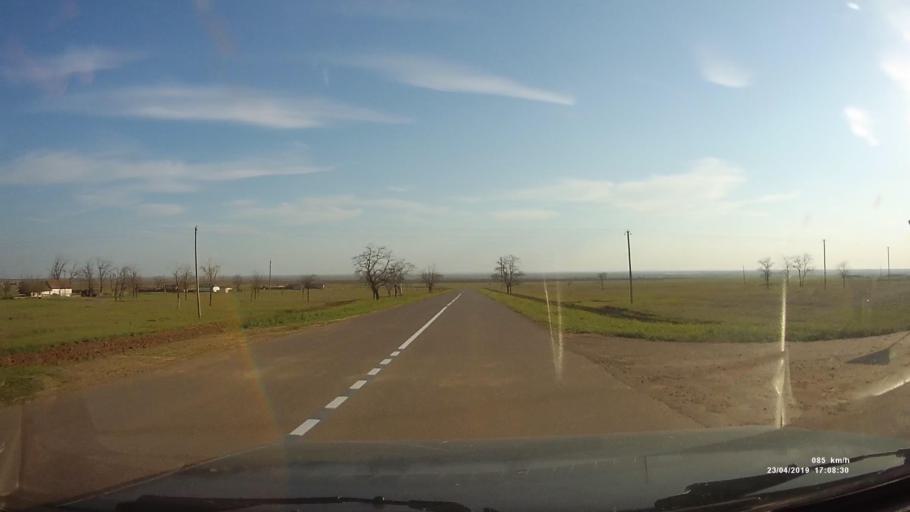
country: RU
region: Kalmykiya
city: Priyutnoye
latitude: 46.2706
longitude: 43.4872
